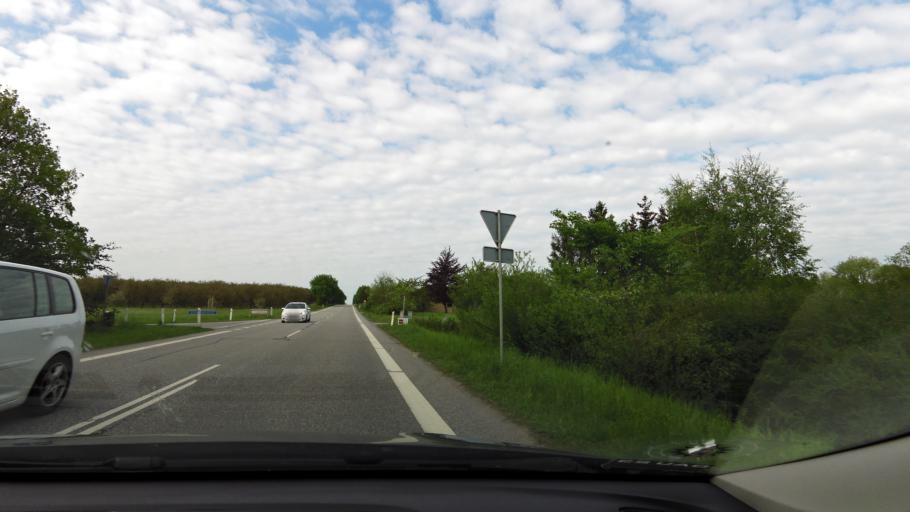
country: DK
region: South Denmark
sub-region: Nyborg Kommune
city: Nyborg
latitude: 55.3077
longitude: 10.7272
